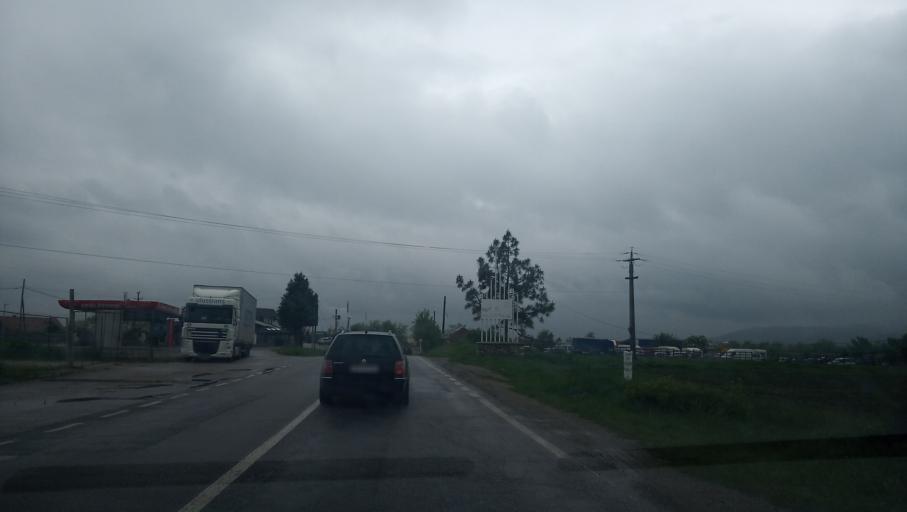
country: RO
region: Alba
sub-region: Municipiul Sebes
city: Sebes
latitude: 45.9480
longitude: 23.5859
